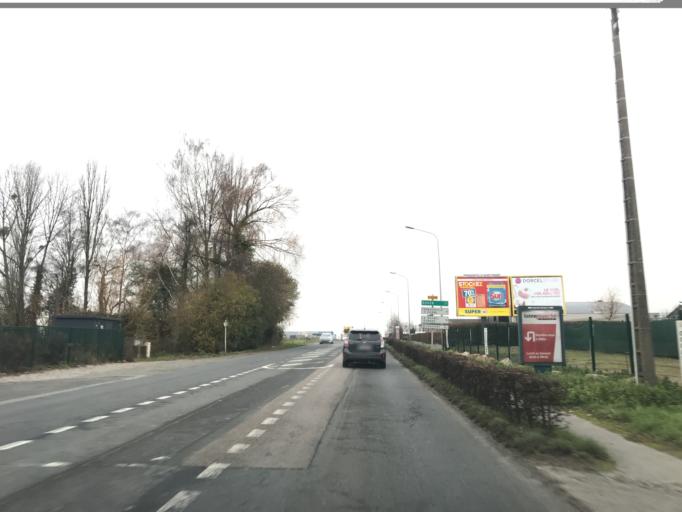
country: FR
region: Haute-Normandie
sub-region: Departement de la Seine-Maritime
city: Boos
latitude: 49.3902
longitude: 1.1979
